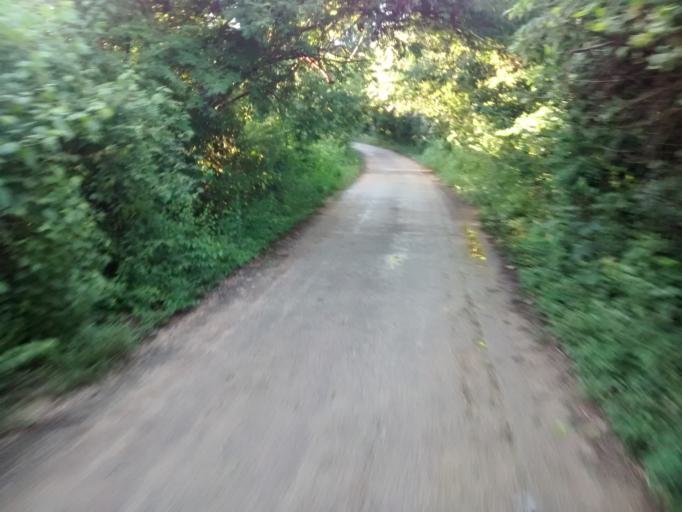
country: MX
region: Yucatan
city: Valladolid
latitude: 20.7239
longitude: -88.2280
